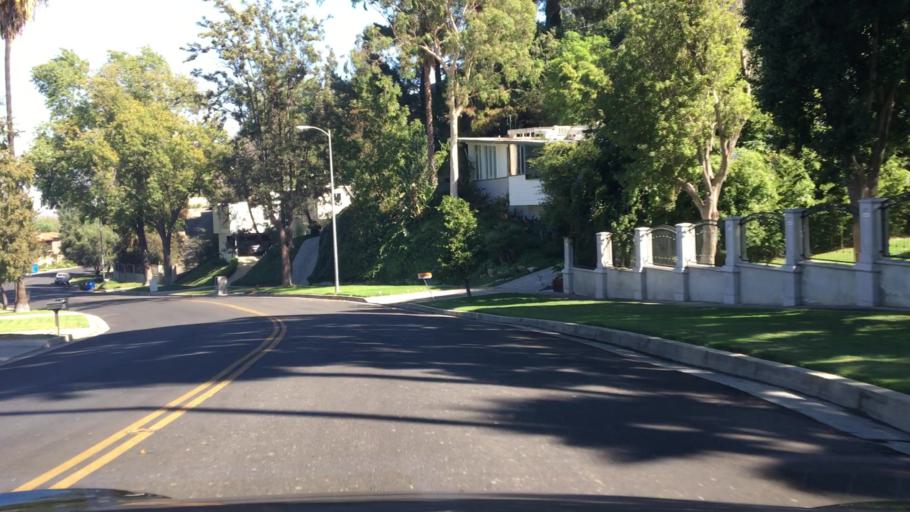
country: US
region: California
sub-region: Los Angeles County
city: Sherman Oaks
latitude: 34.1433
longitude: -118.4393
